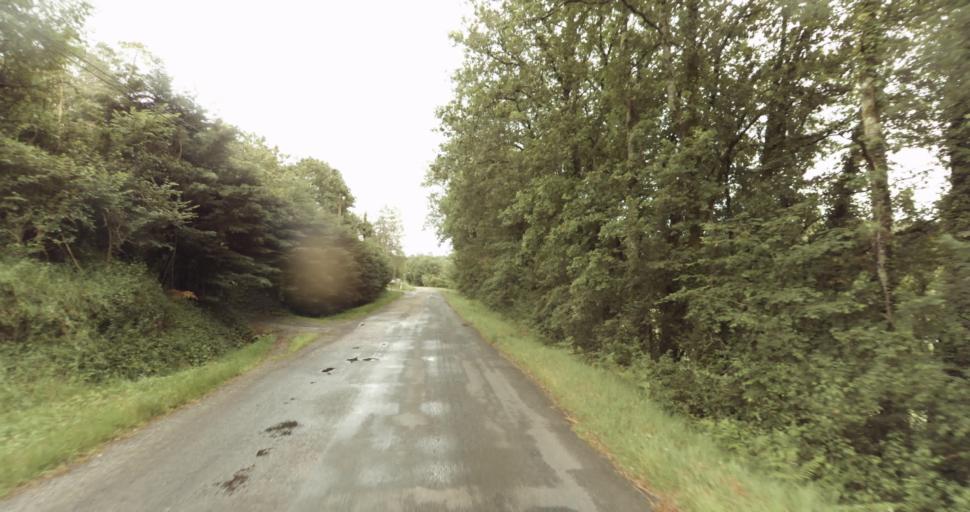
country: FR
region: Aquitaine
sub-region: Departement de la Dordogne
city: Belves
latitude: 44.7578
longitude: 0.9216
